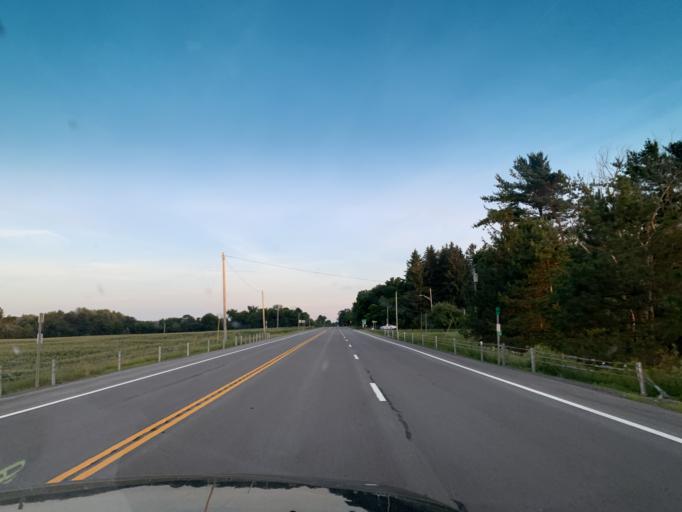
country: US
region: New York
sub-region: Oneida County
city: Chadwicks
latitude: 42.9393
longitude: -75.2520
